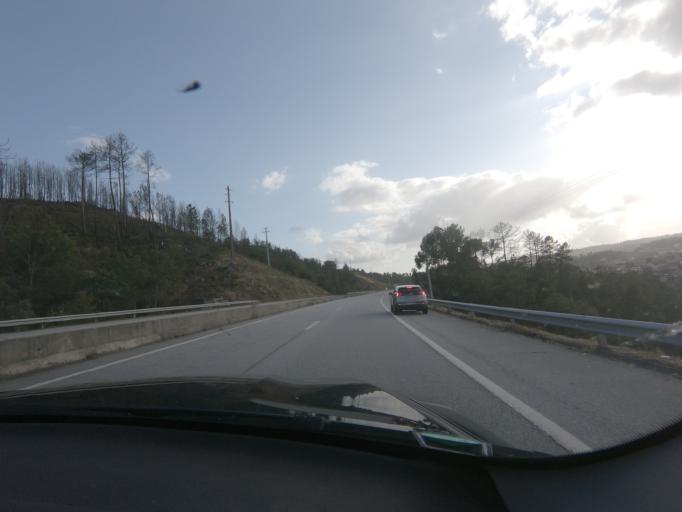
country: PT
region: Viseu
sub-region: Viseu
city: Viseu
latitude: 40.6080
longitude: -7.9693
